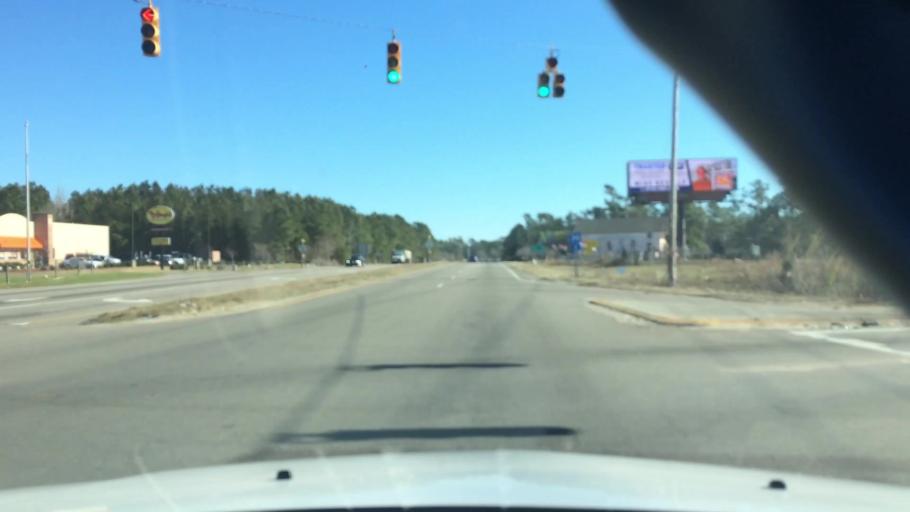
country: US
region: North Carolina
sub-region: Brunswick County
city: Shallotte
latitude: 34.0172
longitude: -78.2731
